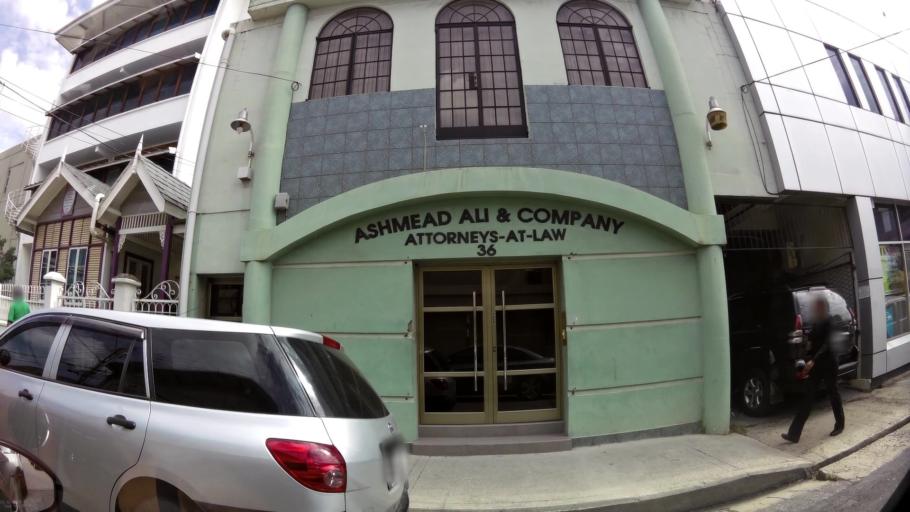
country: TT
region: City of Port of Spain
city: Port-of-Spain
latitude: 10.6544
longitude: -61.5130
